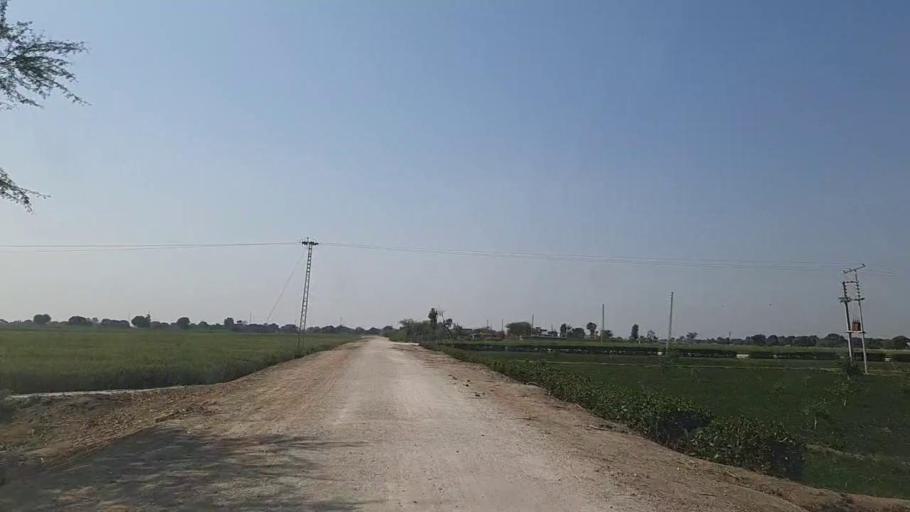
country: PK
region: Sindh
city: Naukot
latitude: 24.8616
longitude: 69.4237
